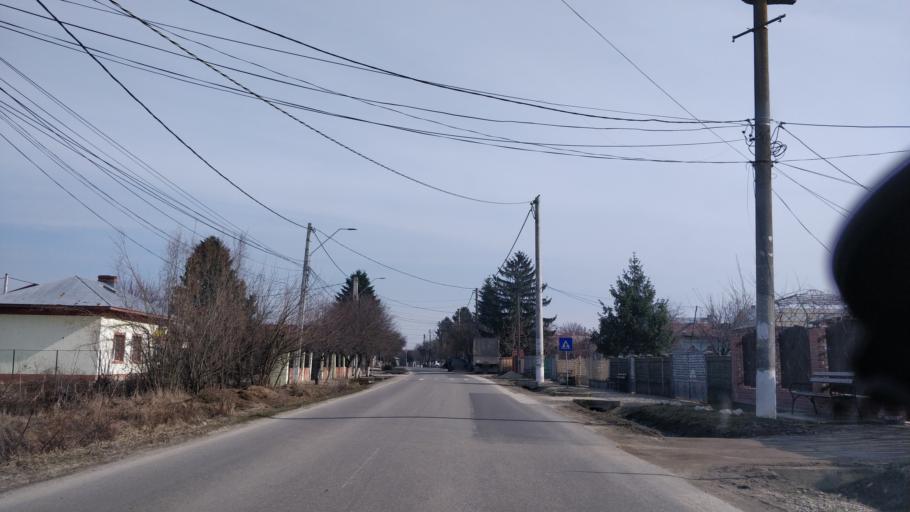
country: RO
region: Giurgiu
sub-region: Comuna Ulmi
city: Ulmi
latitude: 44.4829
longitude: 25.8004
